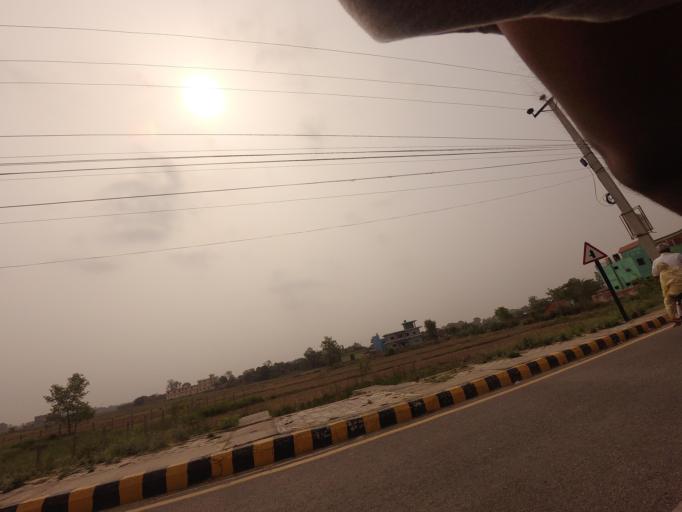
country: IN
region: Uttar Pradesh
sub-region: Maharajganj
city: Nautanwa
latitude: 27.4853
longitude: 83.2843
